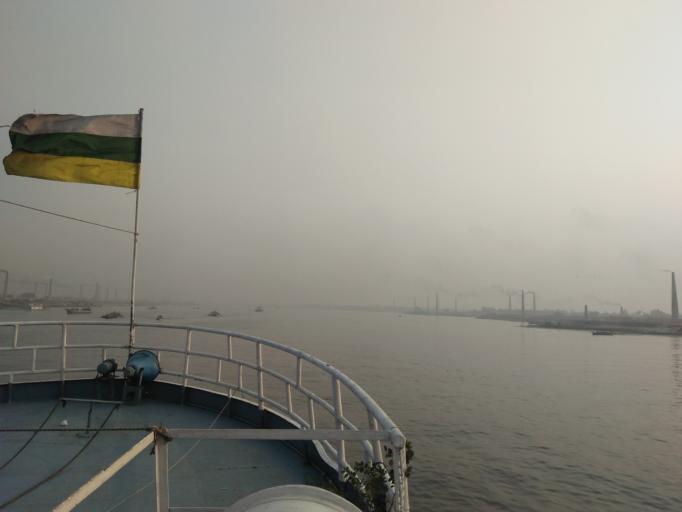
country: BD
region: Dhaka
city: Narayanganj
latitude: 23.6235
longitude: 90.4533
